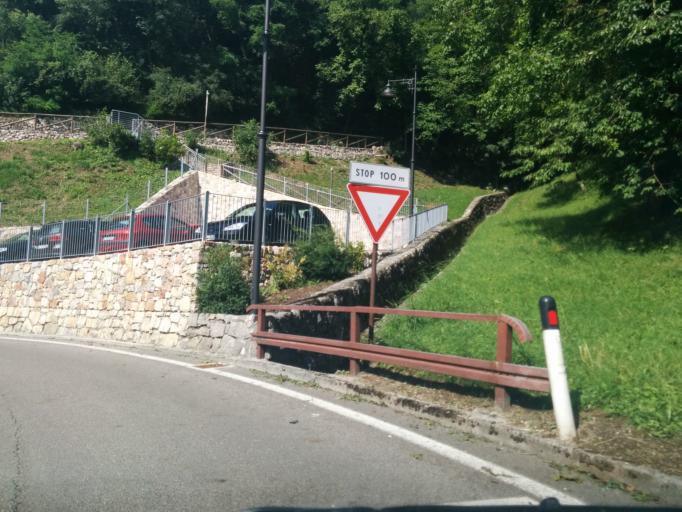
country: IT
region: Trentino-Alto Adige
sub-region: Provincia di Trento
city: Tenno
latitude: 45.9300
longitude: 10.8247
